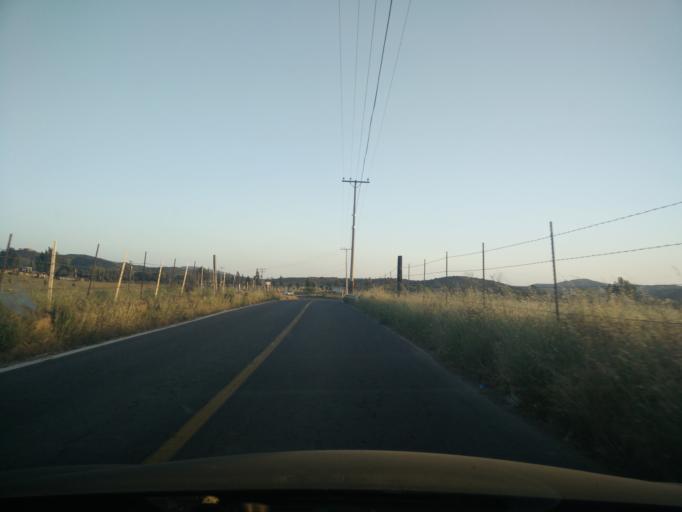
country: MX
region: Baja California
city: El Sauzal
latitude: 32.0193
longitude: -116.6744
